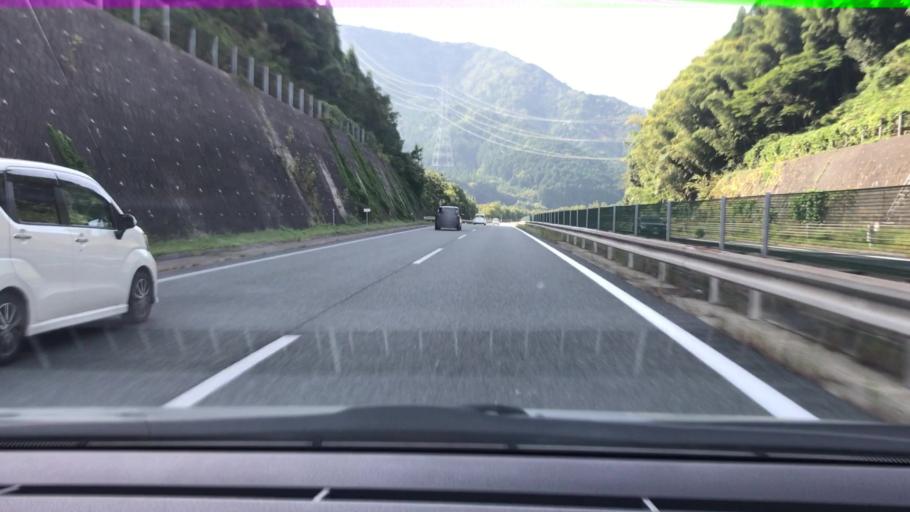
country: JP
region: Hyogo
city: Sasayama
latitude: 35.0408
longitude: 135.1826
